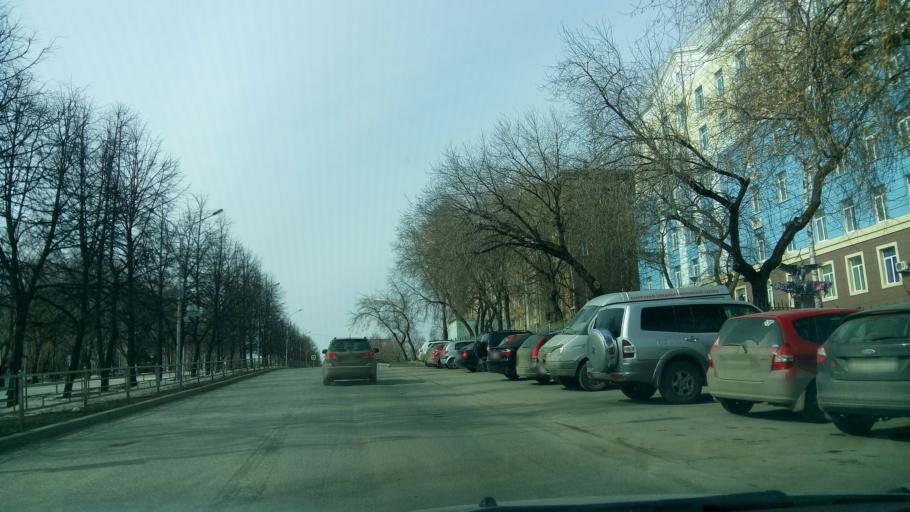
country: RU
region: Sverdlovsk
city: Nizhniy Tagil
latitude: 57.9054
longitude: 59.9711
